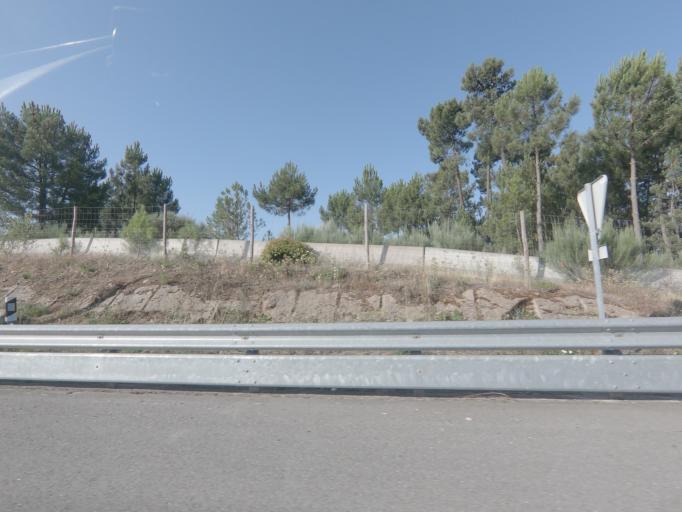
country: PT
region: Vila Real
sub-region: Vila Real
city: Vila Real
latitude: 41.2936
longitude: -7.6943
